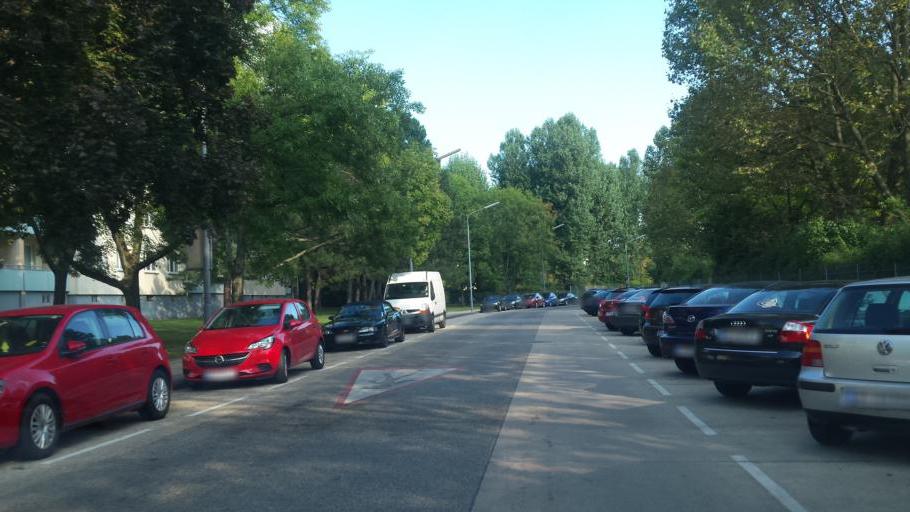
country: AT
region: Lower Austria
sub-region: Politischer Bezirk Wien-Umgebung
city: Leopoldsdorf
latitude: 48.1496
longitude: 16.3840
